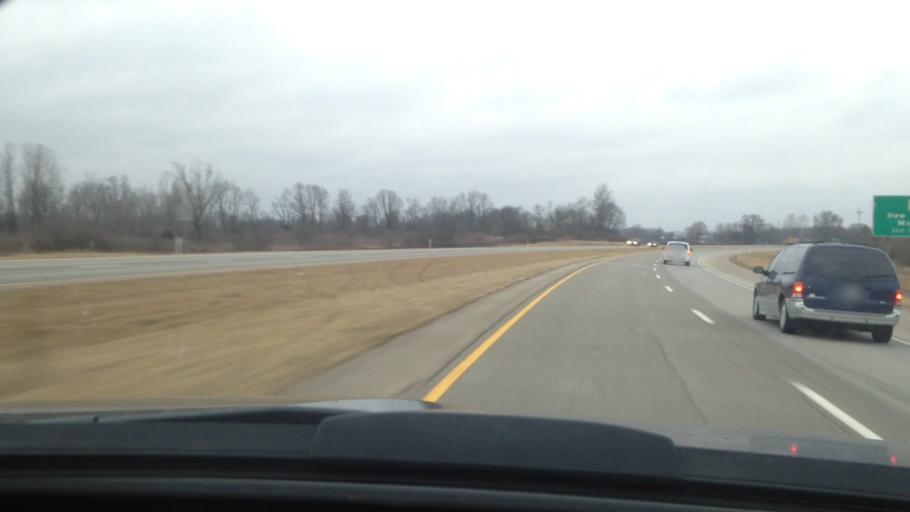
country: US
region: Indiana
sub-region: Delaware County
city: Muncie
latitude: 40.1559
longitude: -85.3537
